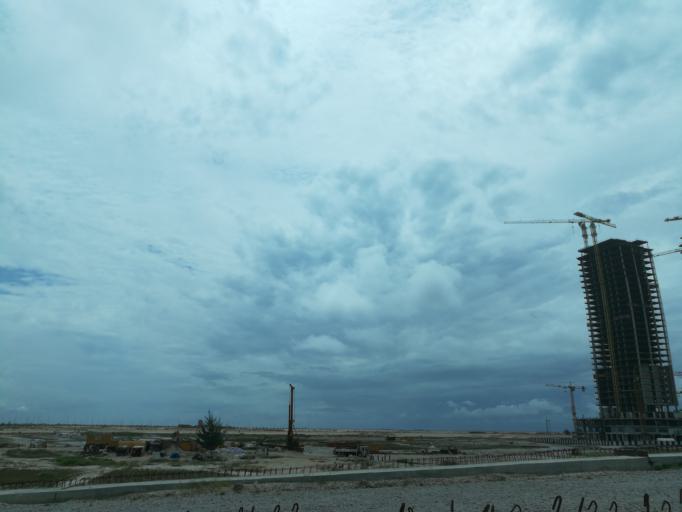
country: NG
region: Lagos
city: Lagos
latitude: 6.4058
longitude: 3.4040
